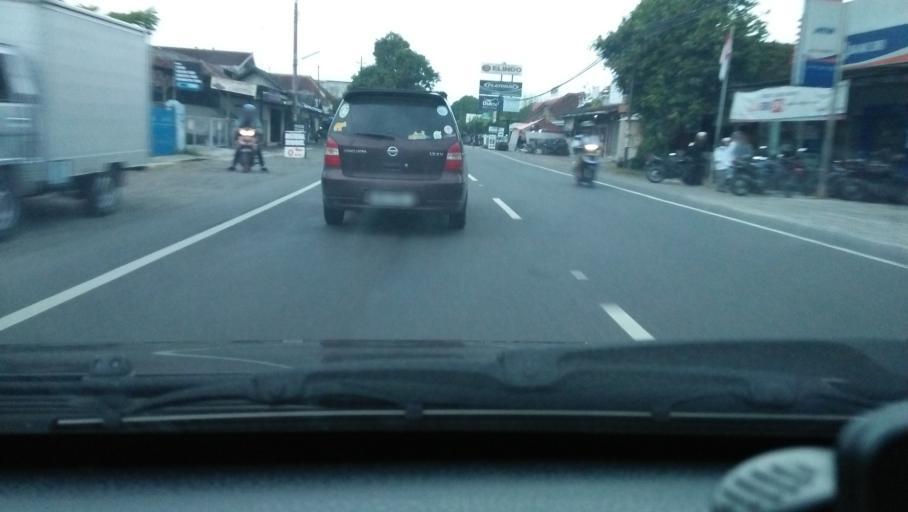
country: ID
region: Central Java
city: Magelang
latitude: -7.4276
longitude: 110.2299
